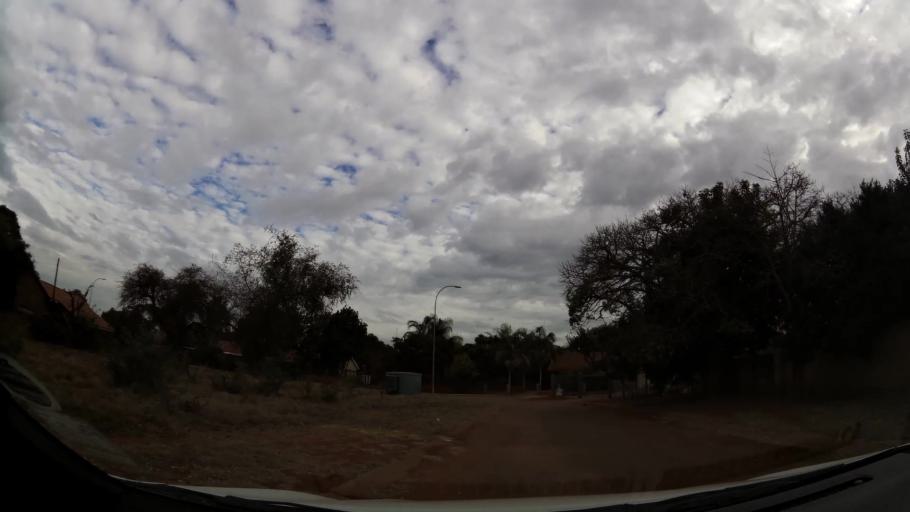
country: ZA
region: Limpopo
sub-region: Waterberg District Municipality
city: Modimolle
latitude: -24.5233
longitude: 28.7056
